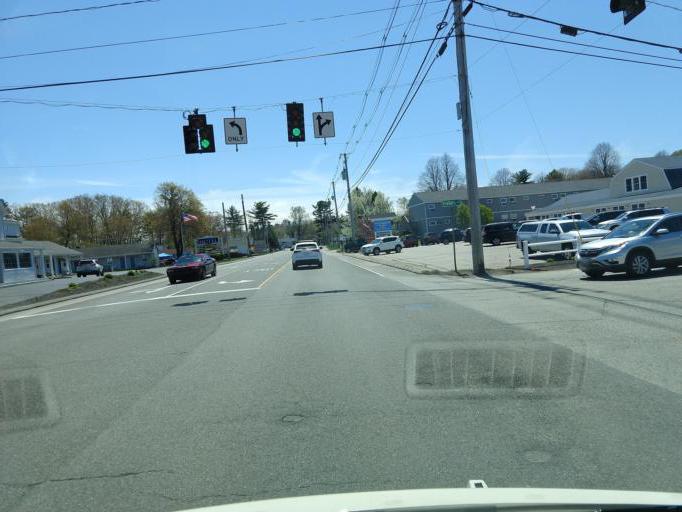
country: US
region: Maine
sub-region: York County
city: Ogunquit
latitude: 43.2754
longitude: -70.5973
